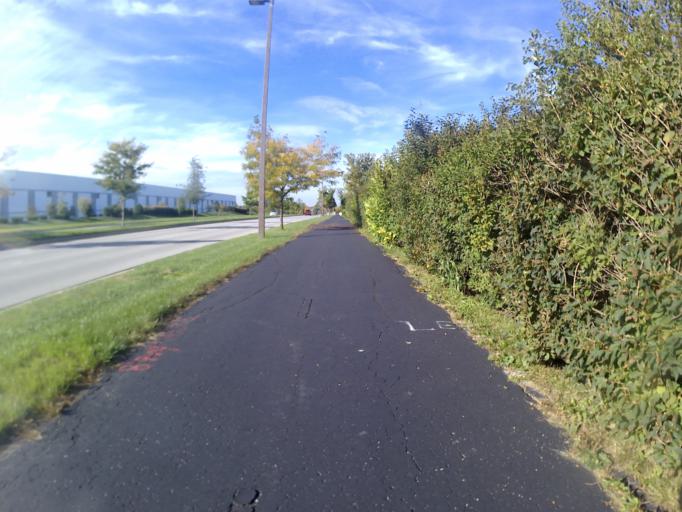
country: US
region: Illinois
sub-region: DuPage County
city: Woodridge
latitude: 41.7150
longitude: -88.0268
